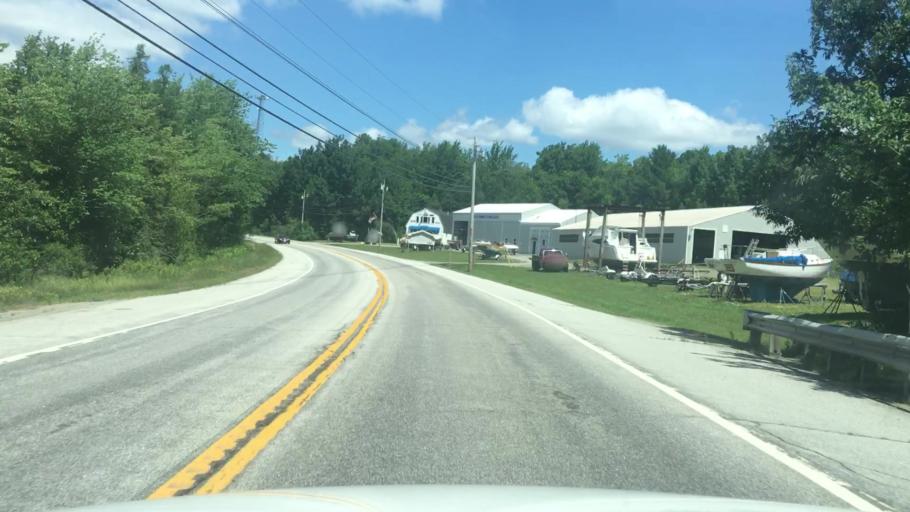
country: US
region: Maine
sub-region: Waldo County
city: Northport
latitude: 44.3532
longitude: -68.9675
